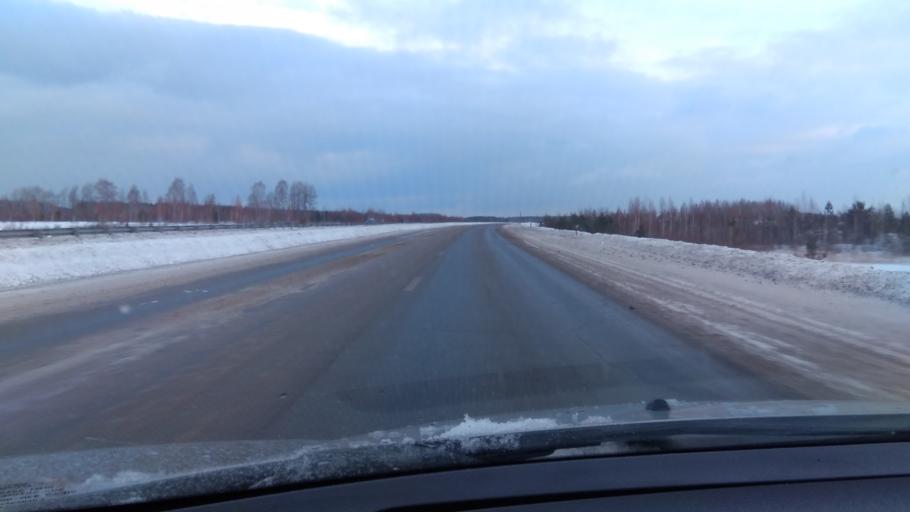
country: RU
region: Sverdlovsk
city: Nev'yansk
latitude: 57.5162
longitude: 60.1794
